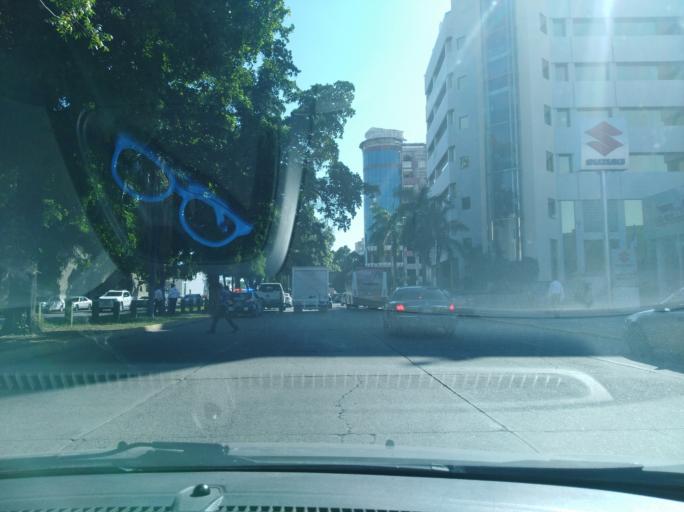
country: MX
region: Sinaloa
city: Culiacan
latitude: 24.7954
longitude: -107.4120
